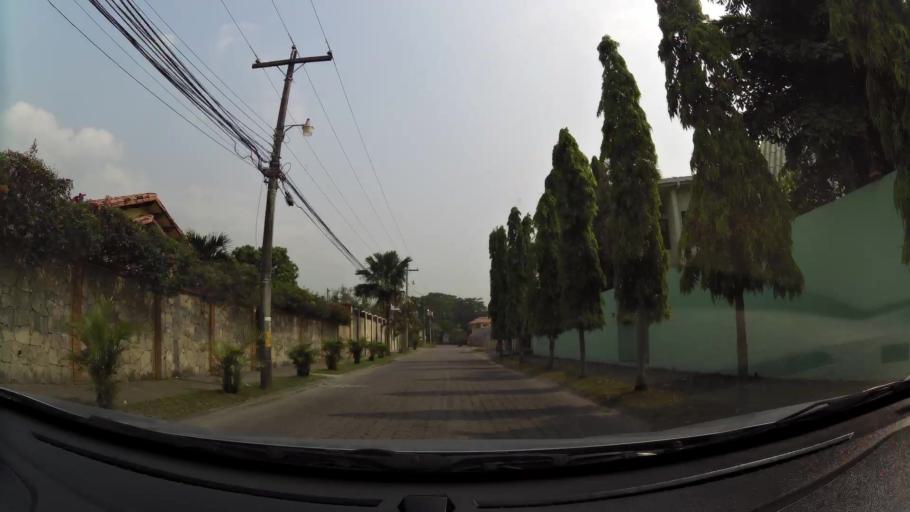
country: HN
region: Cortes
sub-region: San Pedro Sula
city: Pena Blanca
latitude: 15.5368
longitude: -88.0310
